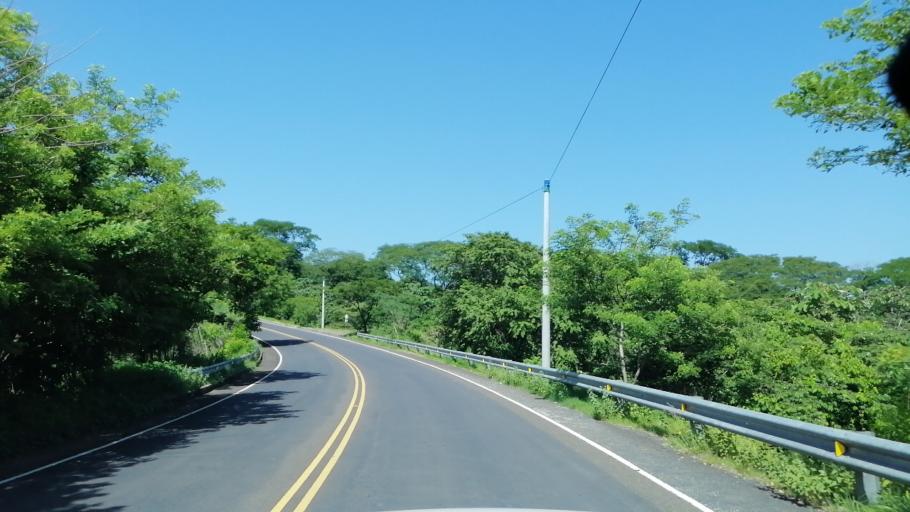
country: HN
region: Lempira
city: La Virtud
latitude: 13.9853
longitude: -88.7570
